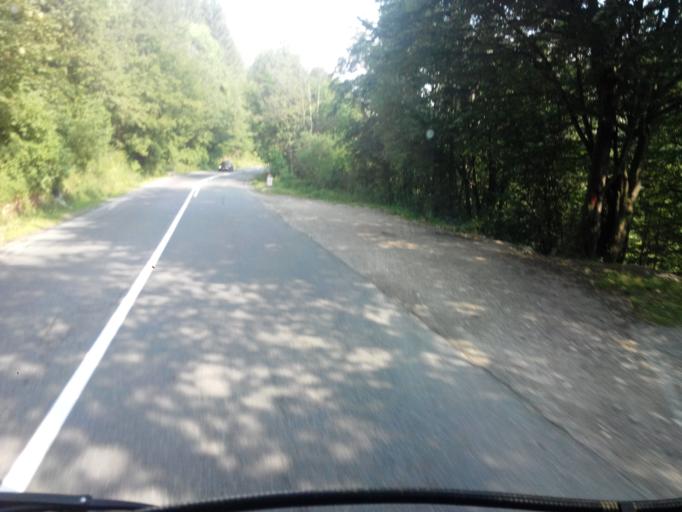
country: RO
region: Brasov
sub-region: Oras Predeal
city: Predeal
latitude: 45.5227
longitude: 25.5077
